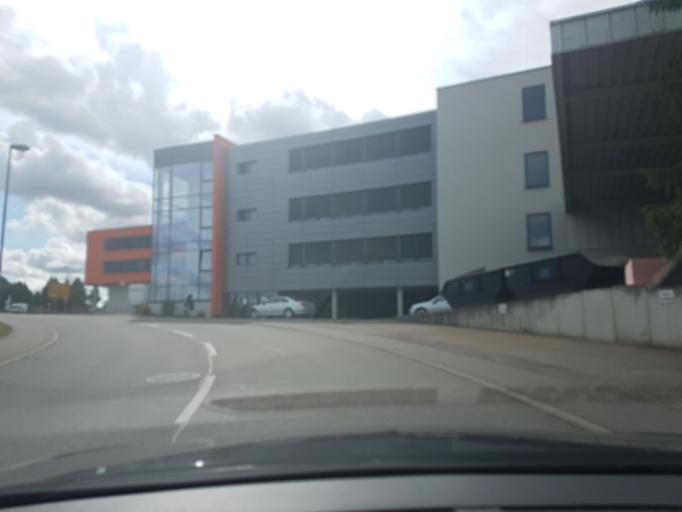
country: DE
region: Baden-Wuerttemberg
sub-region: Regierungsbezirk Stuttgart
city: Neuenstadt am Kocher
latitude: 49.2383
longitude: 9.3414
